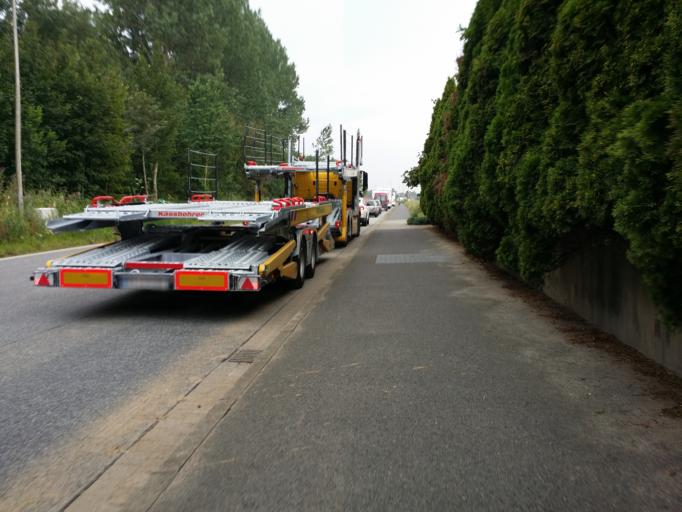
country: DE
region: Schleswig-Holstein
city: Blomesche Wildnis
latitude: 53.8076
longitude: 9.4197
